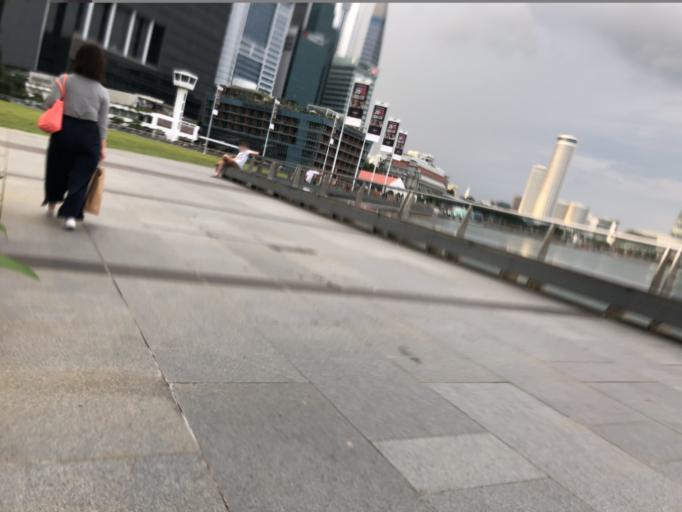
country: SG
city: Singapore
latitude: 1.2814
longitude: 103.8548
